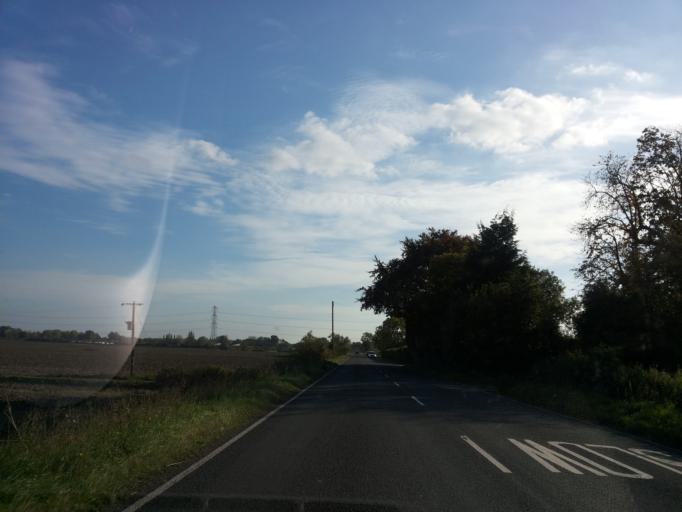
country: GB
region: England
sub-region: Doncaster
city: Hatfield
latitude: 53.6311
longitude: -0.9815
